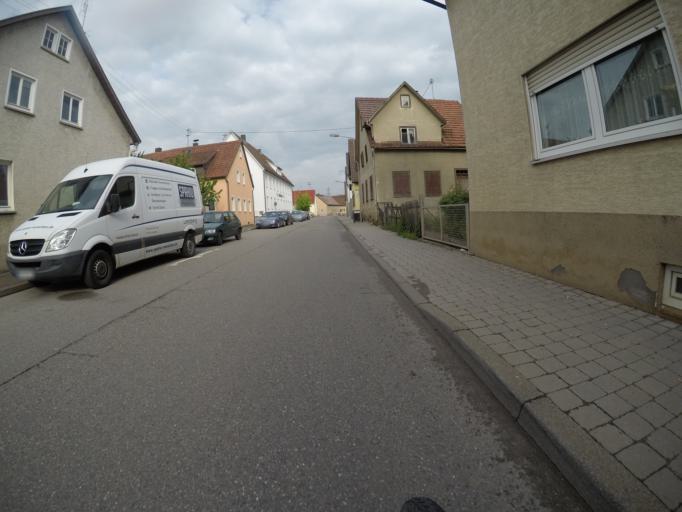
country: DE
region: Baden-Wuerttemberg
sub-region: Regierungsbezirk Stuttgart
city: Magstadt
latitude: 48.7430
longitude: 8.9593
